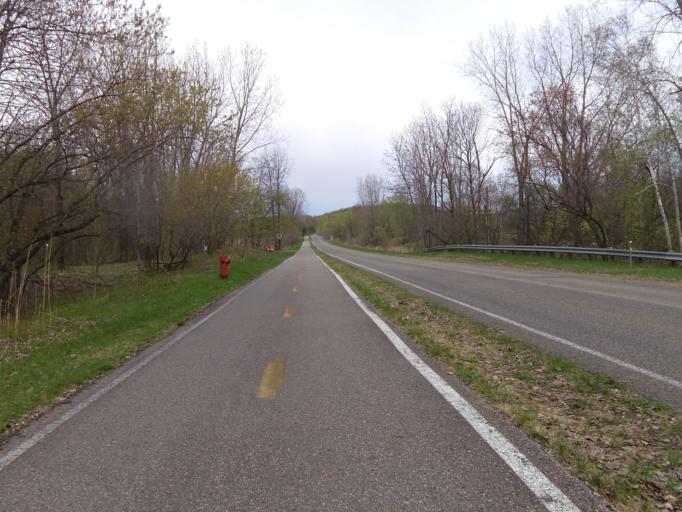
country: CA
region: Quebec
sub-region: Laurentides
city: Oka
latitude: 45.4835
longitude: -74.0270
